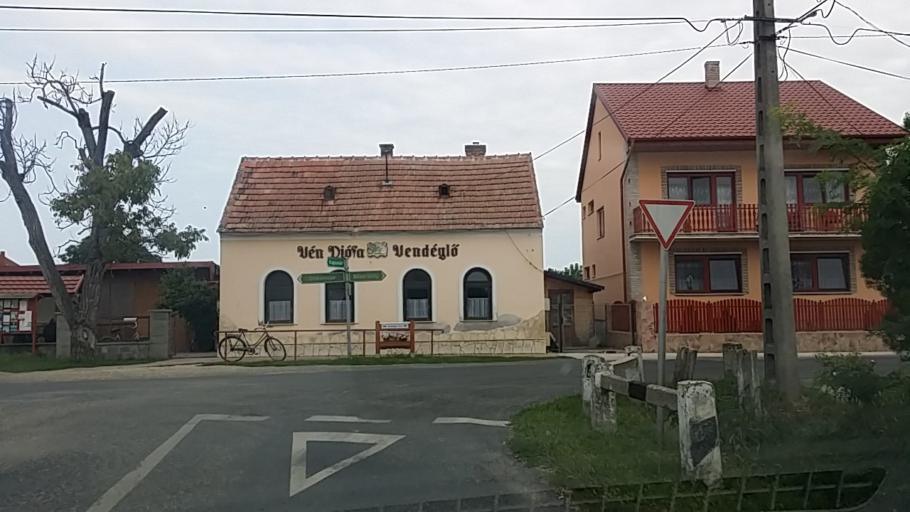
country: HU
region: Gyor-Moson-Sopron
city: Kapuvar
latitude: 47.6403
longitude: 17.0747
